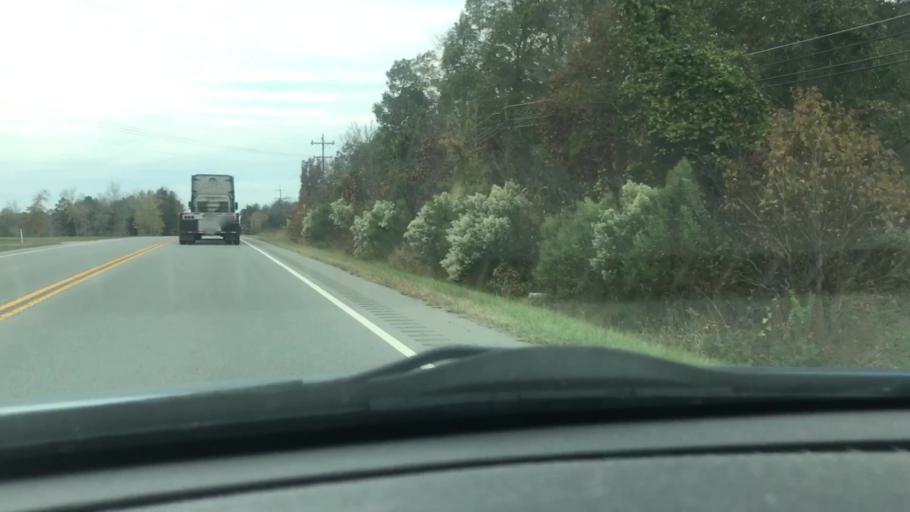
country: US
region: North Carolina
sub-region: Davidson County
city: Thomasville
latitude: 35.7750
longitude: -80.1119
